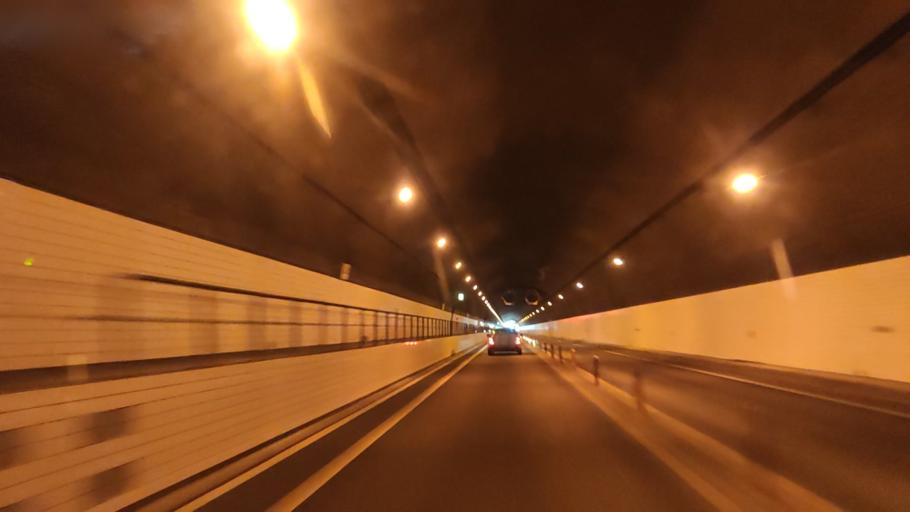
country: JP
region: Tokushima
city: Ikedacho
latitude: 34.0190
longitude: 133.7609
